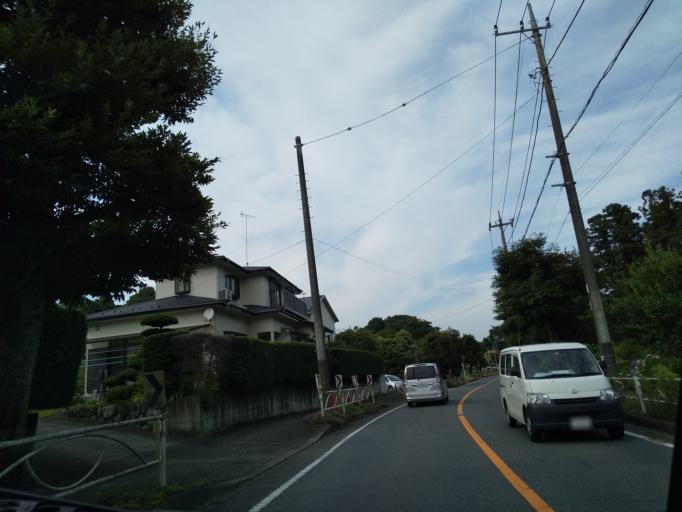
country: JP
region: Kanagawa
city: Atsugi
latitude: 35.4819
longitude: 139.3189
